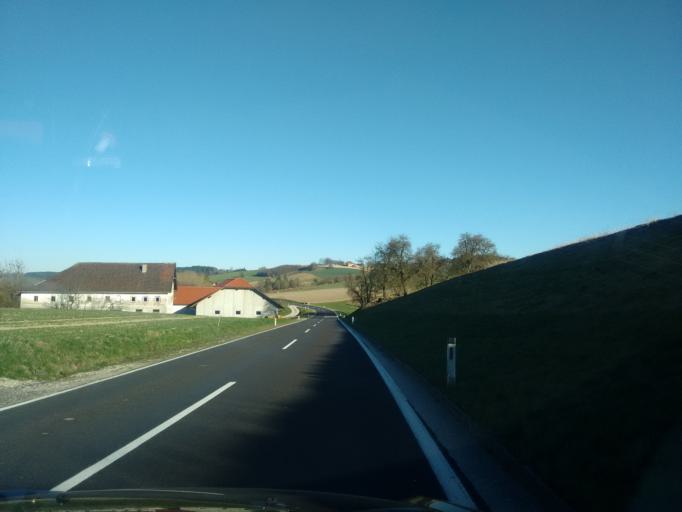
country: AT
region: Upper Austria
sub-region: Wels-Land
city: Offenhausen
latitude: 48.1759
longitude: 13.8306
